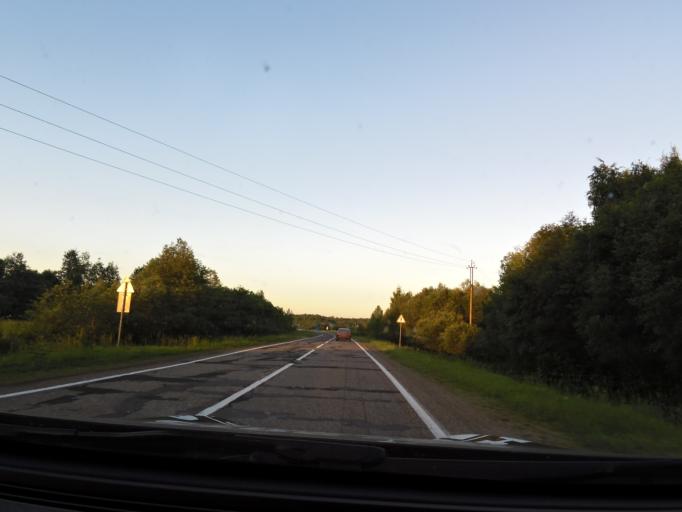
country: RU
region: Jaroslavl
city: Prechistoye
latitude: 58.3605
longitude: 40.5057
